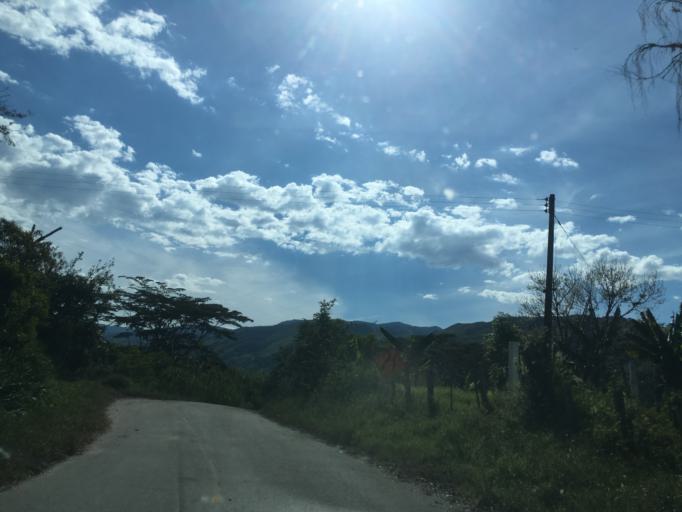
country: CO
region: Santander
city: Oiba
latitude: 6.2049
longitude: -73.1743
